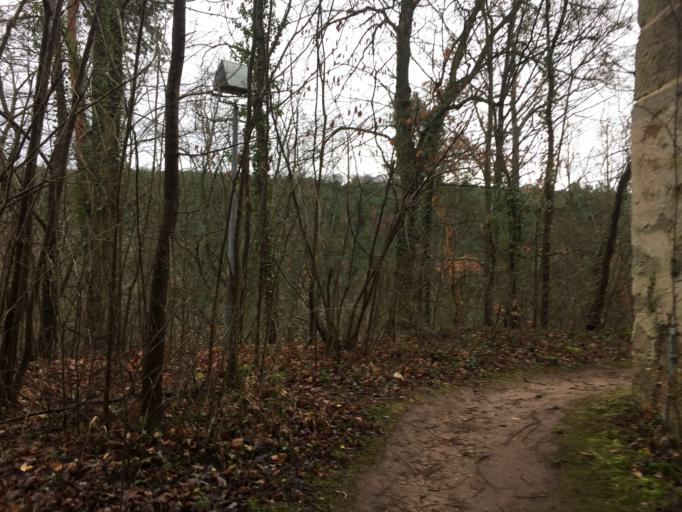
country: DE
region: Rheinland-Pfalz
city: Altleiningen
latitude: 49.5116
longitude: 8.0832
